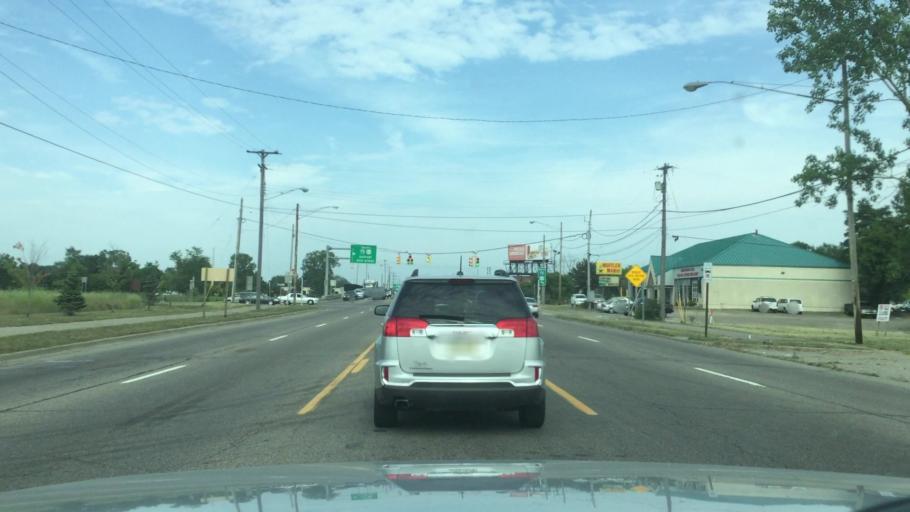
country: US
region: Michigan
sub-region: Genesee County
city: Flint
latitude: 43.0021
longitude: -83.7520
